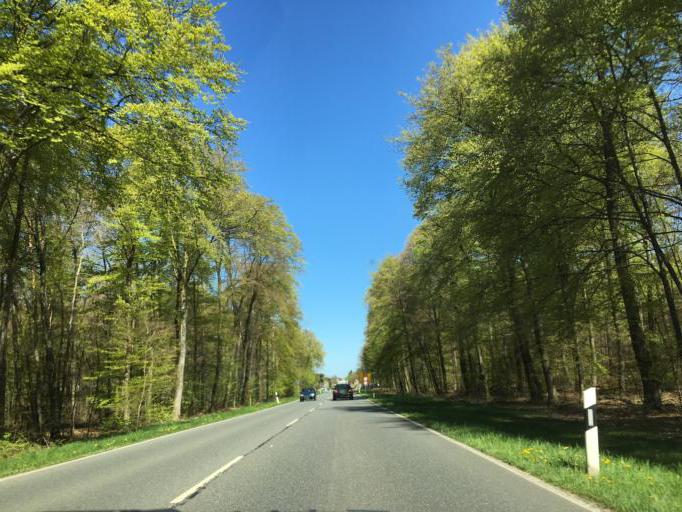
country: DE
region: Hesse
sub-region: Regierungsbezirk Darmstadt
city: Neu Isenburg
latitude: 50.0435
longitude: 8.7145
